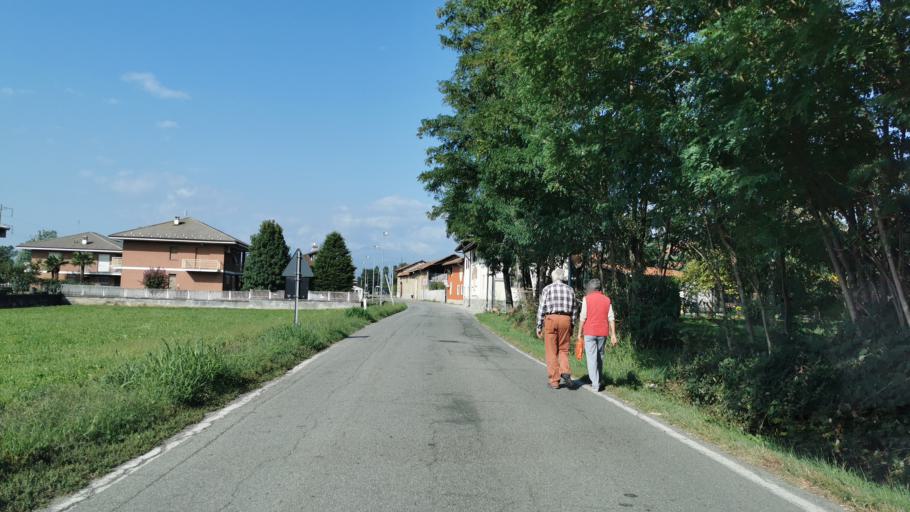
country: IT
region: Piedmont
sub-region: Provincia di Torino
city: Leini
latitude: 45.2052
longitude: 7.7087
